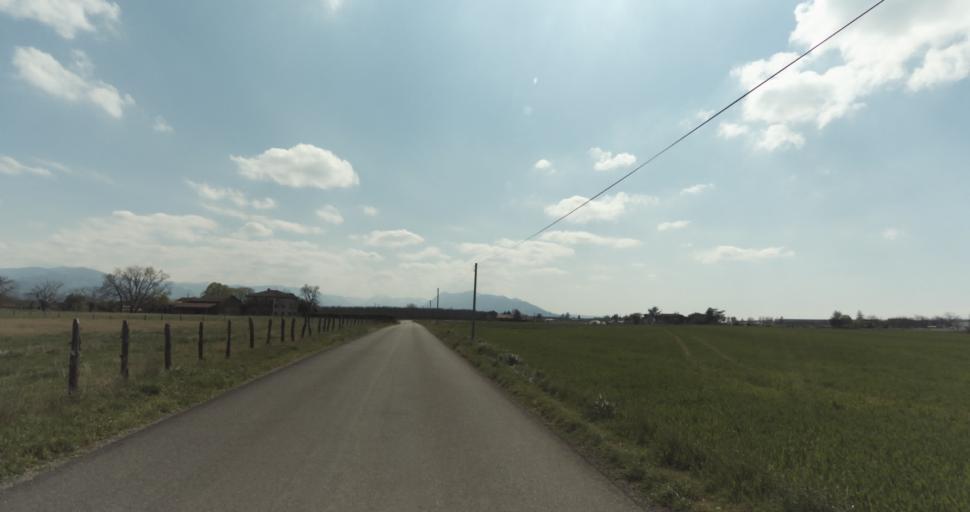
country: FR
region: Rhone-Alpes
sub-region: Departement de l'Isere
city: Saint-Marcellin
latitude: 45.1430
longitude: 5.3088
